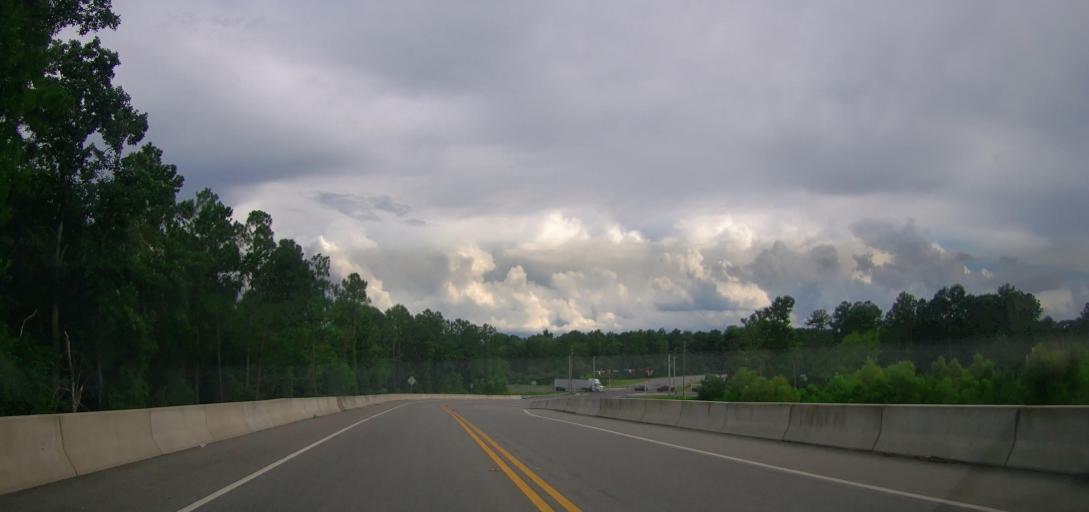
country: US
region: Georgia
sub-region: Wayne County
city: Jesup
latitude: 31.6189
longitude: -81.8939
